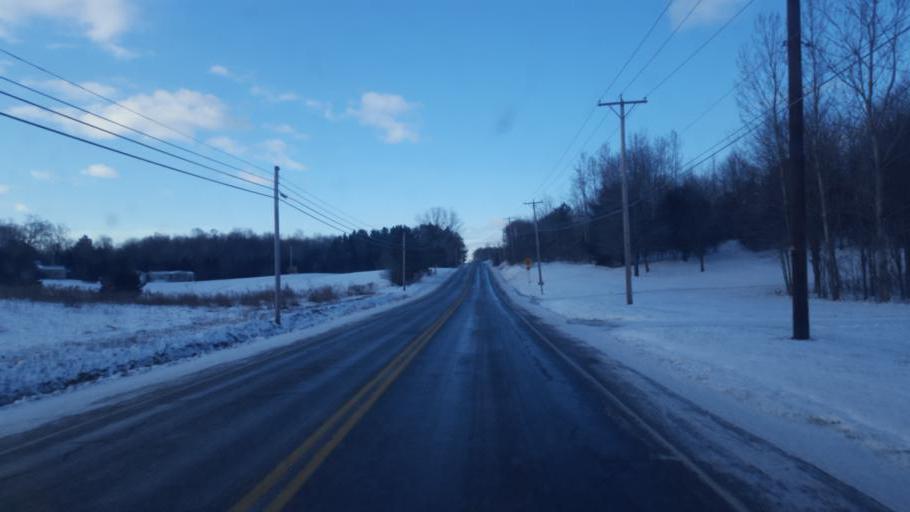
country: US
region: Pennsylvania
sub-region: Mercer County
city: Stoneboro
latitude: 41.4019
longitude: -80.2135
